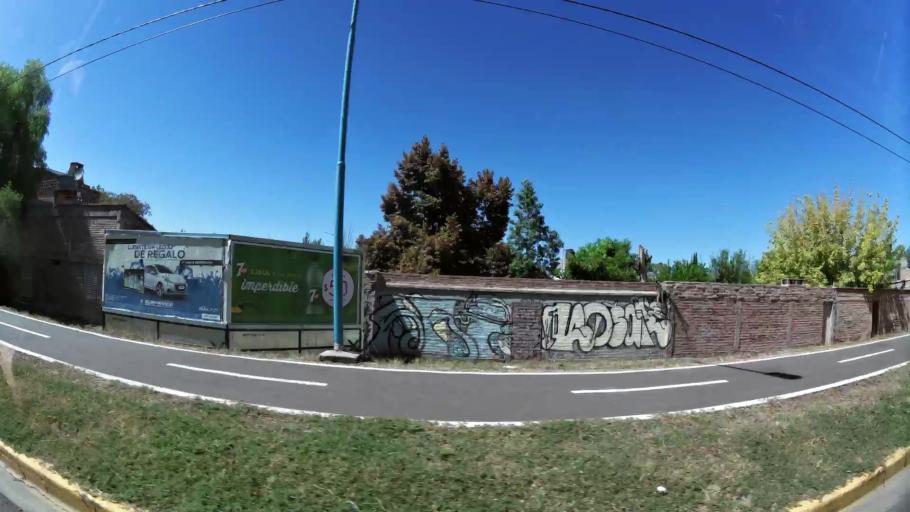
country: AR
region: Mendoza
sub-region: Departamento de Godoy Cruz
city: Godoy Cruz
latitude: -32.9580
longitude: -68.8602
